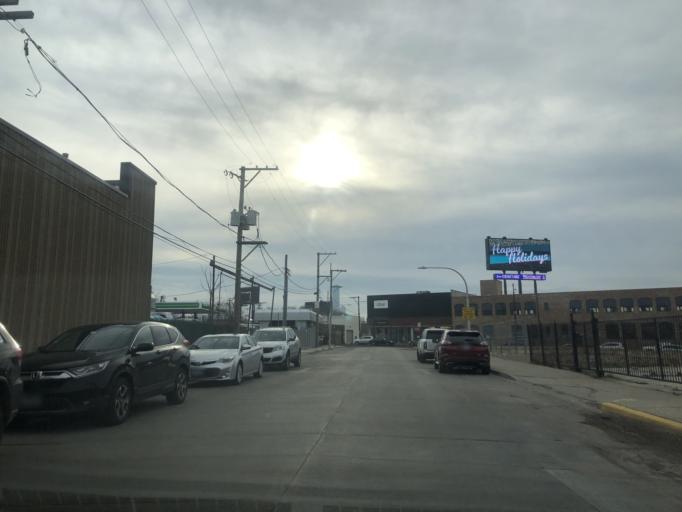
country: US
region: Illinois
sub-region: Cook County
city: Chicago
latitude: 41.9116
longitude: -87.6636
